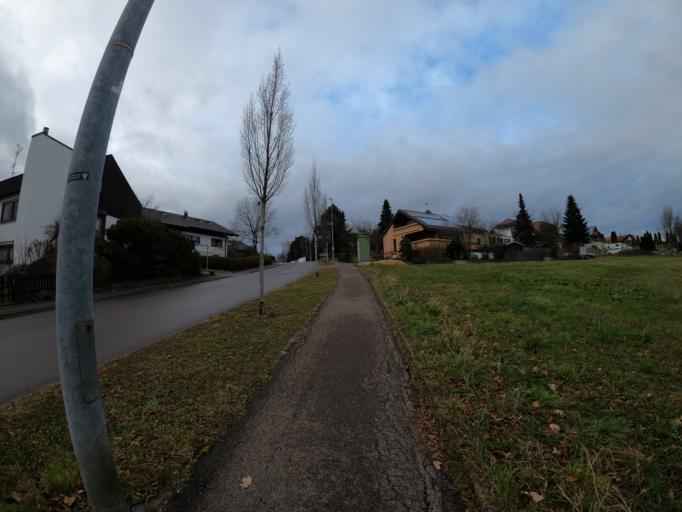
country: DE
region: Baden-Wuerttemberg
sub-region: Regierungsbezirk Stuttgart
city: Waldstetten
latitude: 48.7679
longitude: 9.8323
